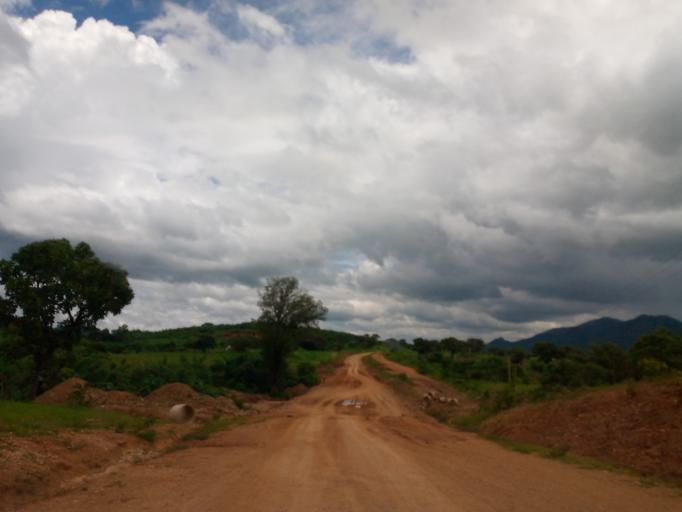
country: ET
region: Oromiya
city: Mendi
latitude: 10.1968
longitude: 35.0916
